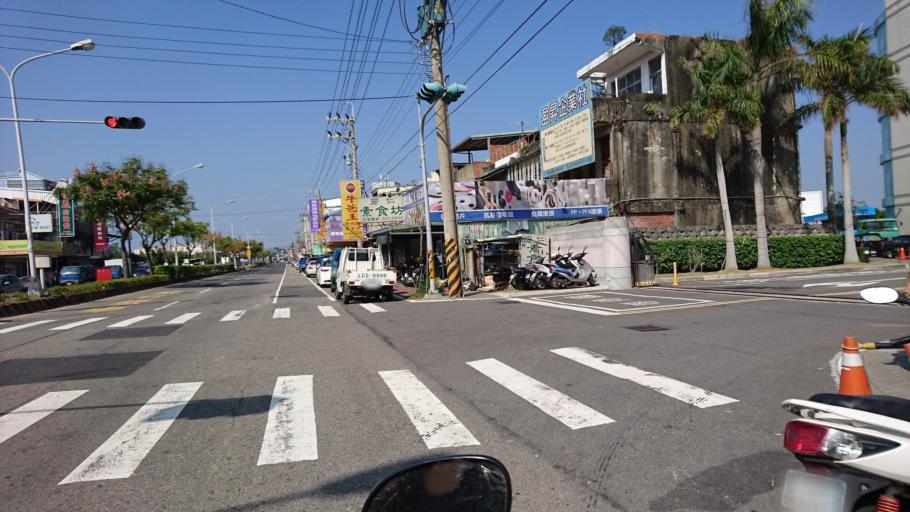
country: TW
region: Taiwan
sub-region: Hsinchu
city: Hsinchu
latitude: 24.7109
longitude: 120.9236
